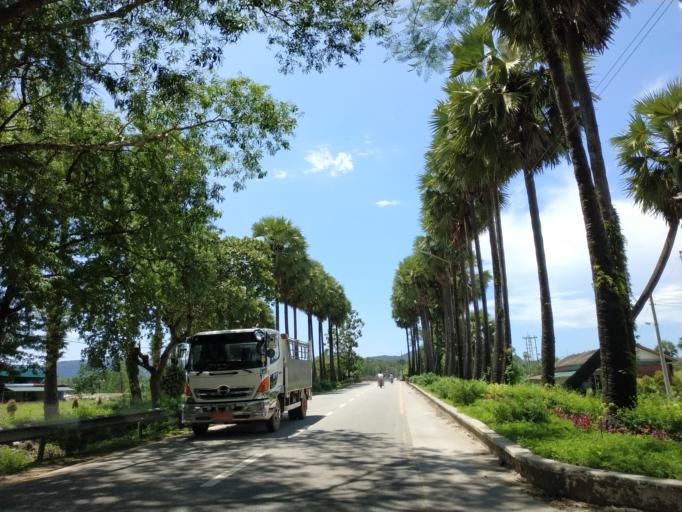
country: MM
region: Tanintharyi
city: Dawei
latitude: 14.0945
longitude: 98.1768
